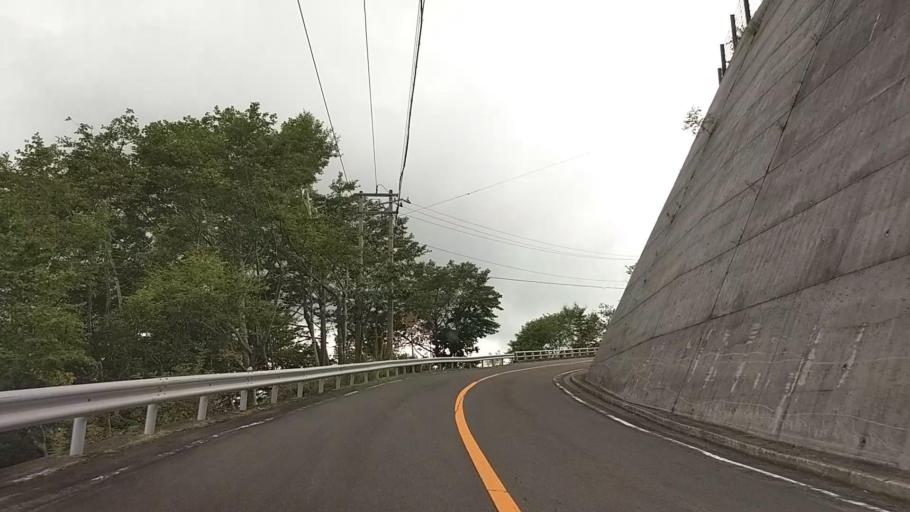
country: JP
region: Tochigi
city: Nikko
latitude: 36.7137
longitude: 139.4837
